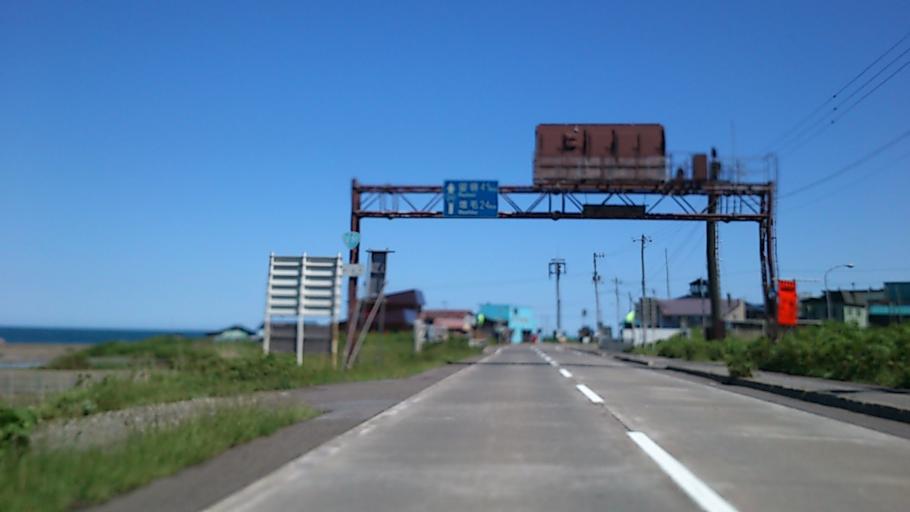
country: JP
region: Hokkaido
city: Rumoi
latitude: 43.7360
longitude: 141.3384
